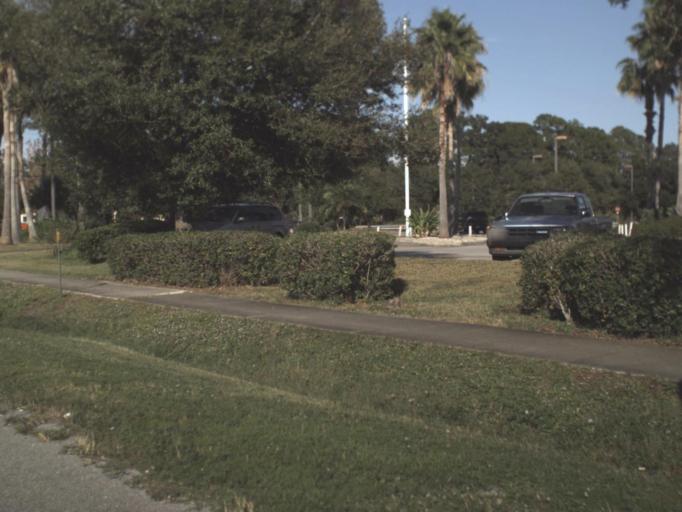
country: US
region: Florida
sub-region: Brevard County
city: June Park
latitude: 28.0712
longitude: -80.6707
